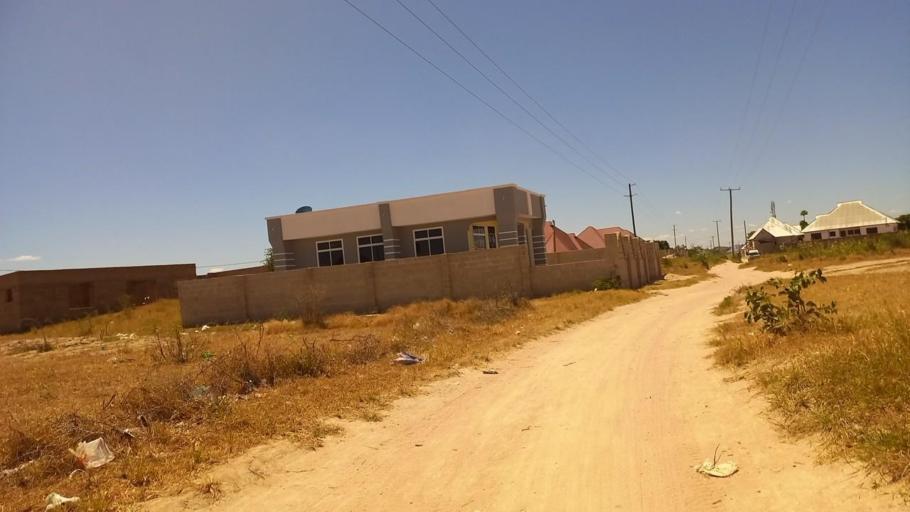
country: TZ
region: Dodoma
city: Dodoma
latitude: -6.1340
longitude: 35.7151
